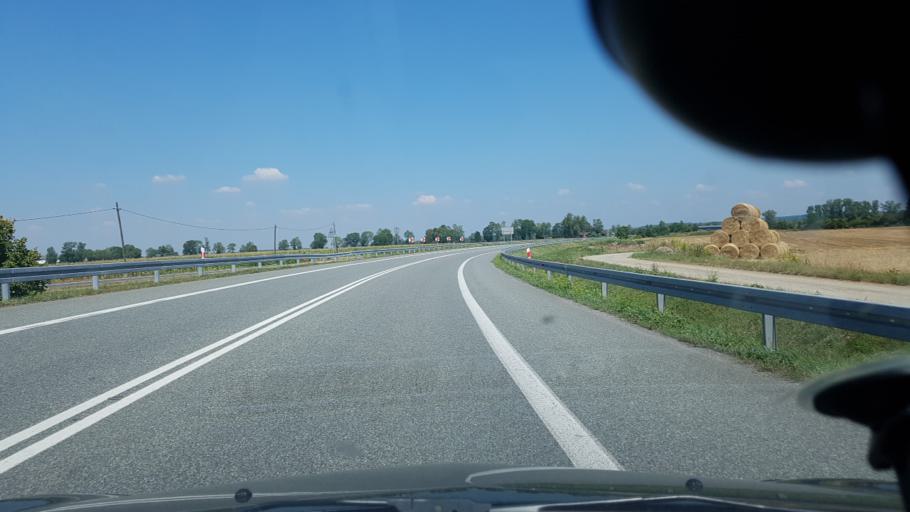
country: PL
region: Silesian Voivodeship
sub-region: Powiat wodzislawski
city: Olza
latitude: 49.9437
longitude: 18.3269
